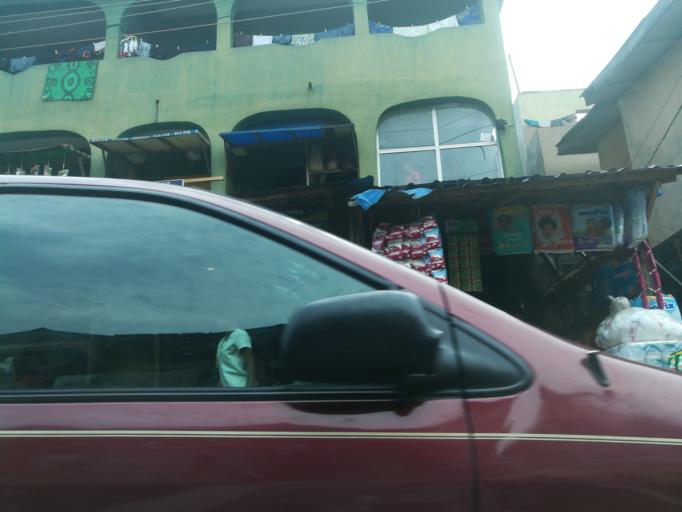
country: NG
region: Lagos
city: Ikorodu
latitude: 6.6179
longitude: 3.5039
